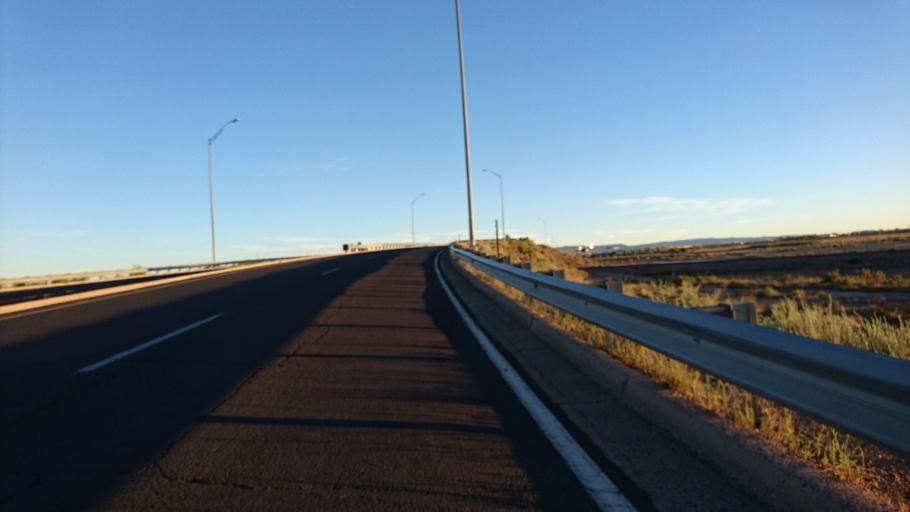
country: US
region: New Mexico
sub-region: Cibola County
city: Grants
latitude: 35.1389
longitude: -107.8285
